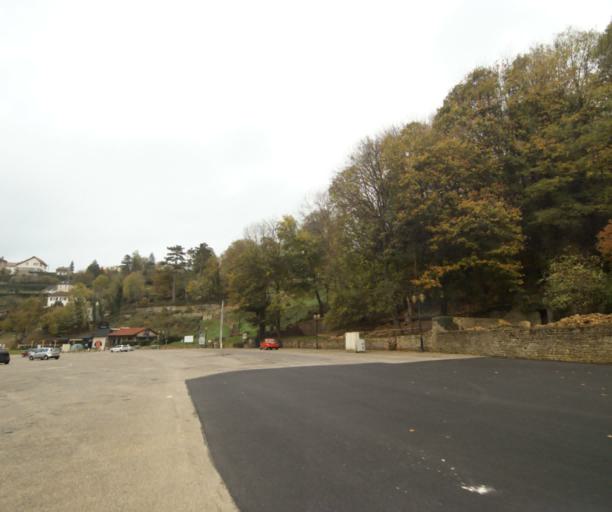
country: FR
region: Lorraine
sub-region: Departement de Meurthe-et-Moselle
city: Briey
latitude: 49.2484
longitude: 5.9353
